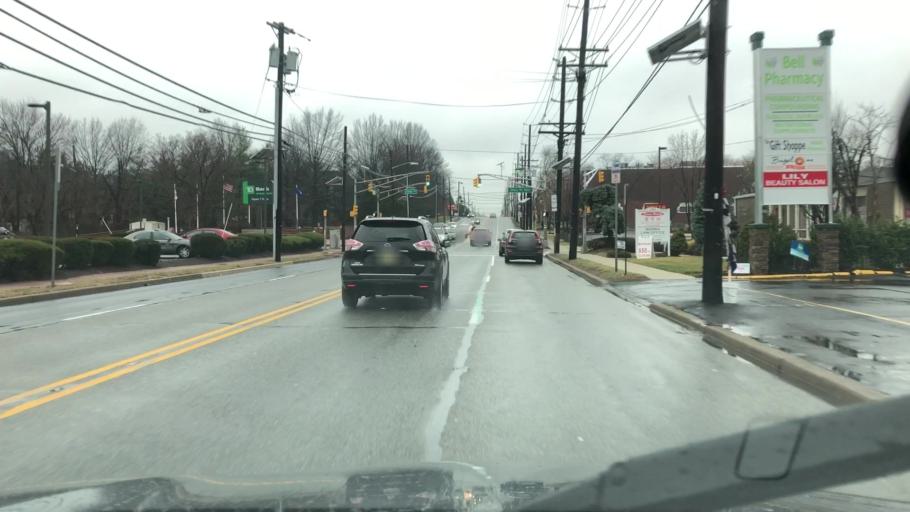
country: US
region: New Jersey
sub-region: Middlesex County
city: Edison
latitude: 40.5174
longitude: -74.3996
